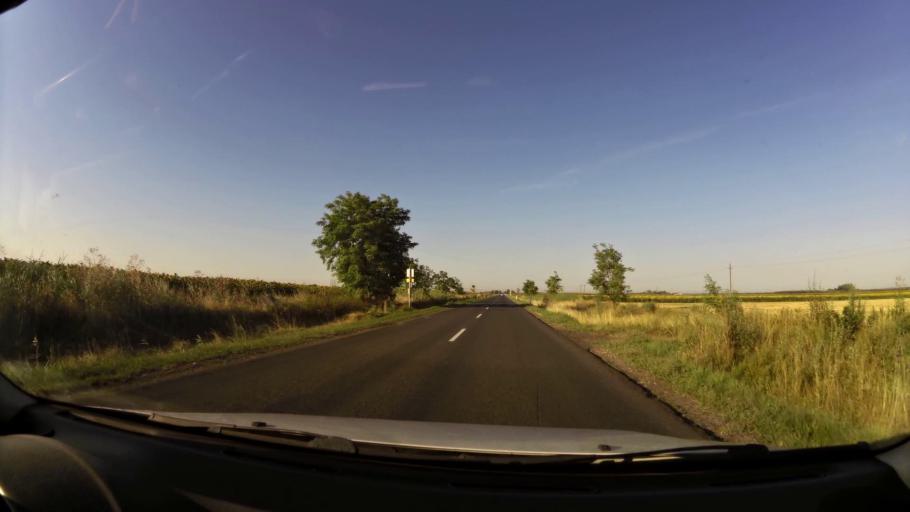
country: HU
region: Pest
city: Tapioszolos
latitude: 47.2504
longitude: 19.8485
